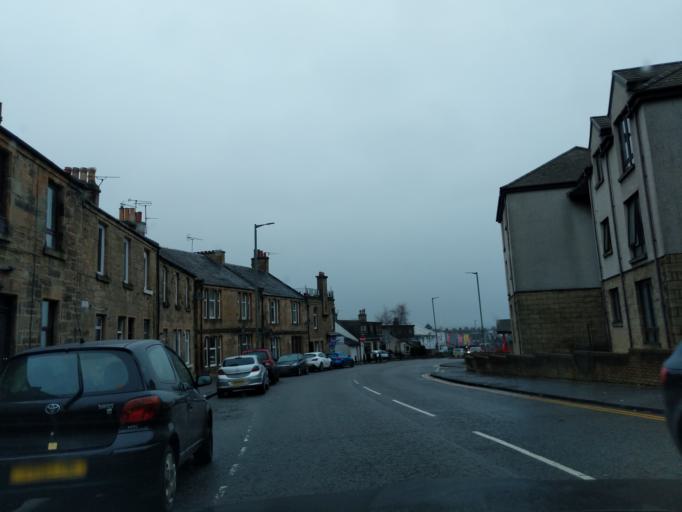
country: GB
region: Scotland
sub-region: Falkirk
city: Falkirk
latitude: 55.9941
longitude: -3.7877
